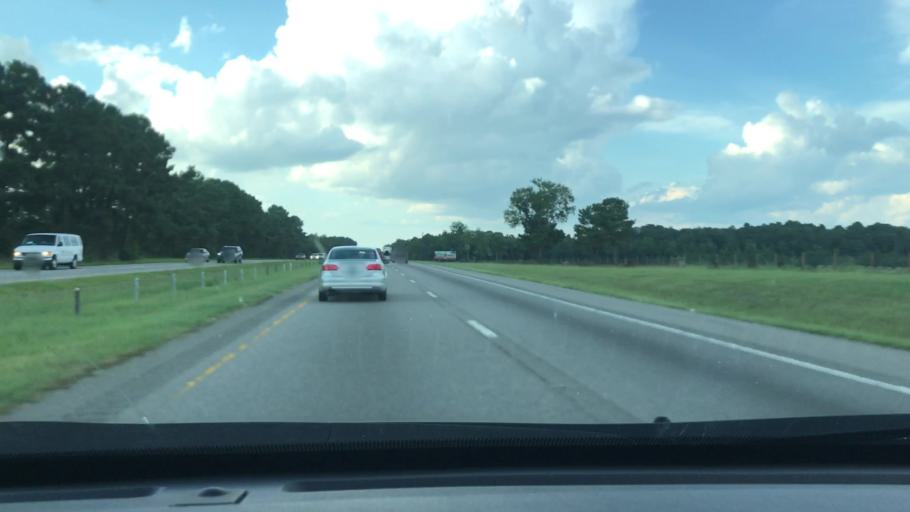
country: US
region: North Carolina
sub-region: Robeson County
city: Saint Pauls
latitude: 34.8650
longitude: -78.9645
